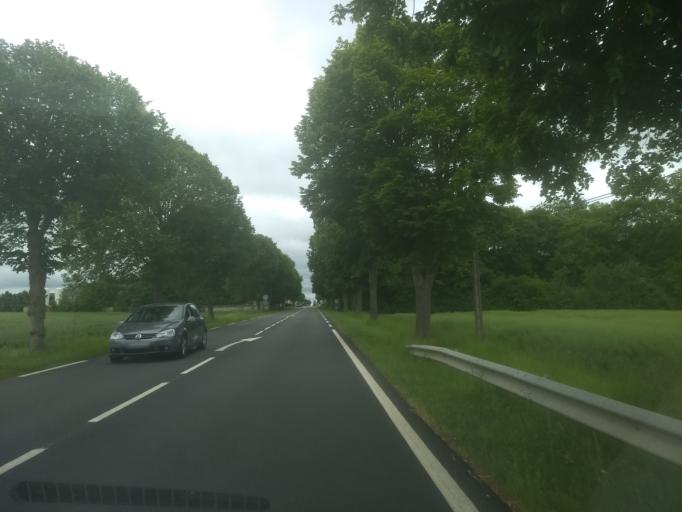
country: FR
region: Centre
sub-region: Departement d'Eure-et-Loir
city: Treon
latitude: 48.6436
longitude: 1.2825
